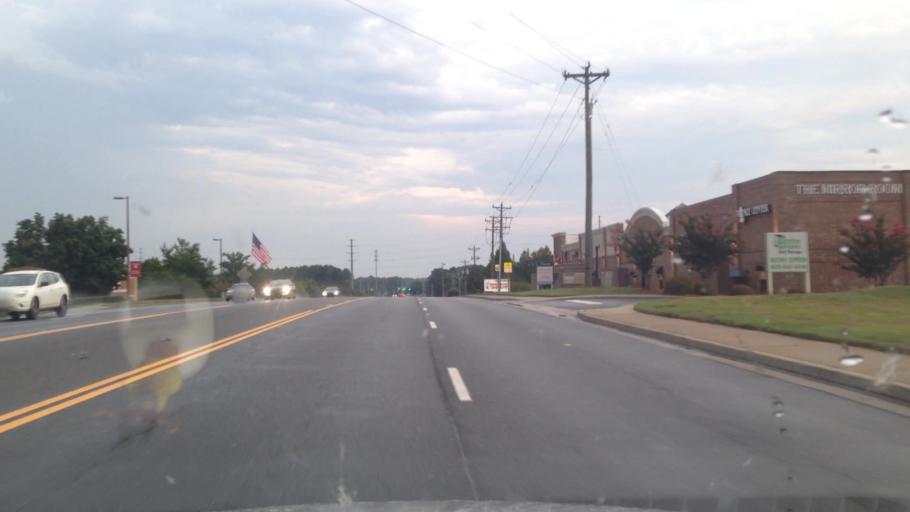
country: US
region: South Carolina
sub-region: York County
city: Fort Mill
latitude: 35.0613
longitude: -80.9628
